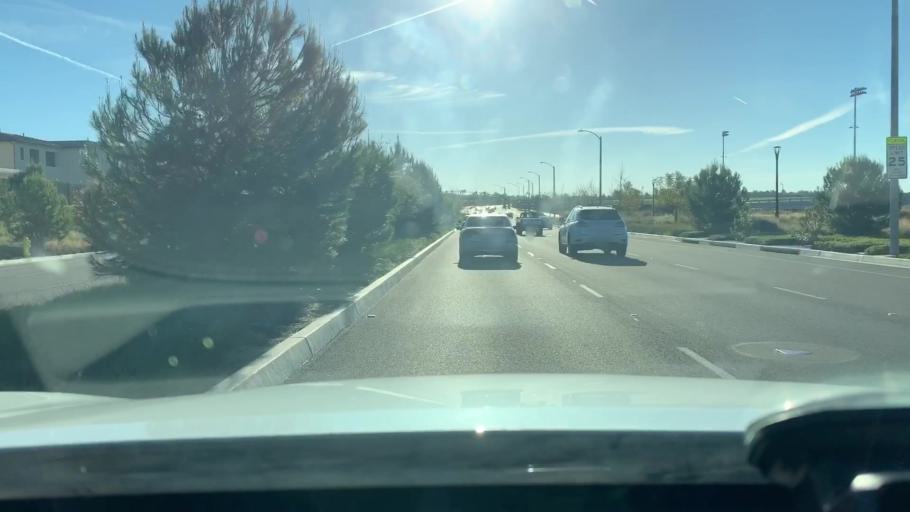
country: US
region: California
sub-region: Orange County
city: Lake Forest
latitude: 33.6744
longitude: -117.7119
